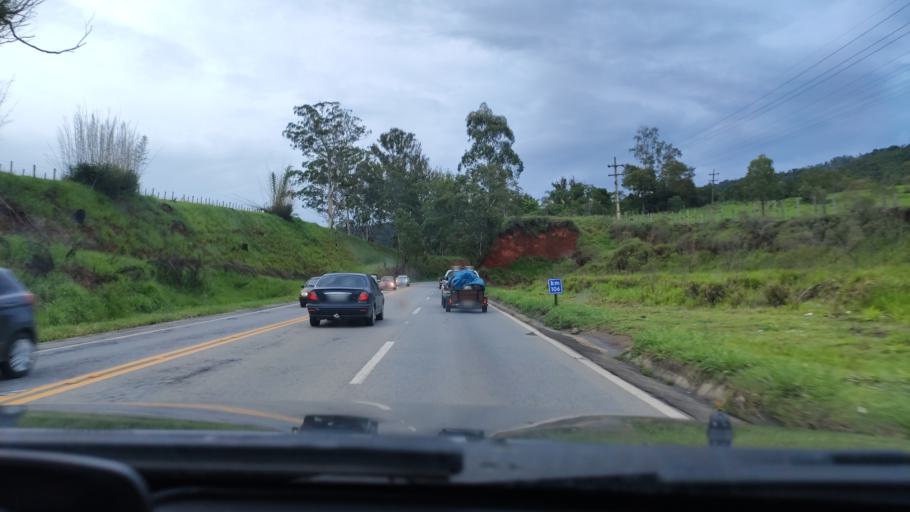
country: BR
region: Sao Paulo
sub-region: Braganca Paulista
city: Braganca Paulista
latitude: -22.8371
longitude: -46.5549
